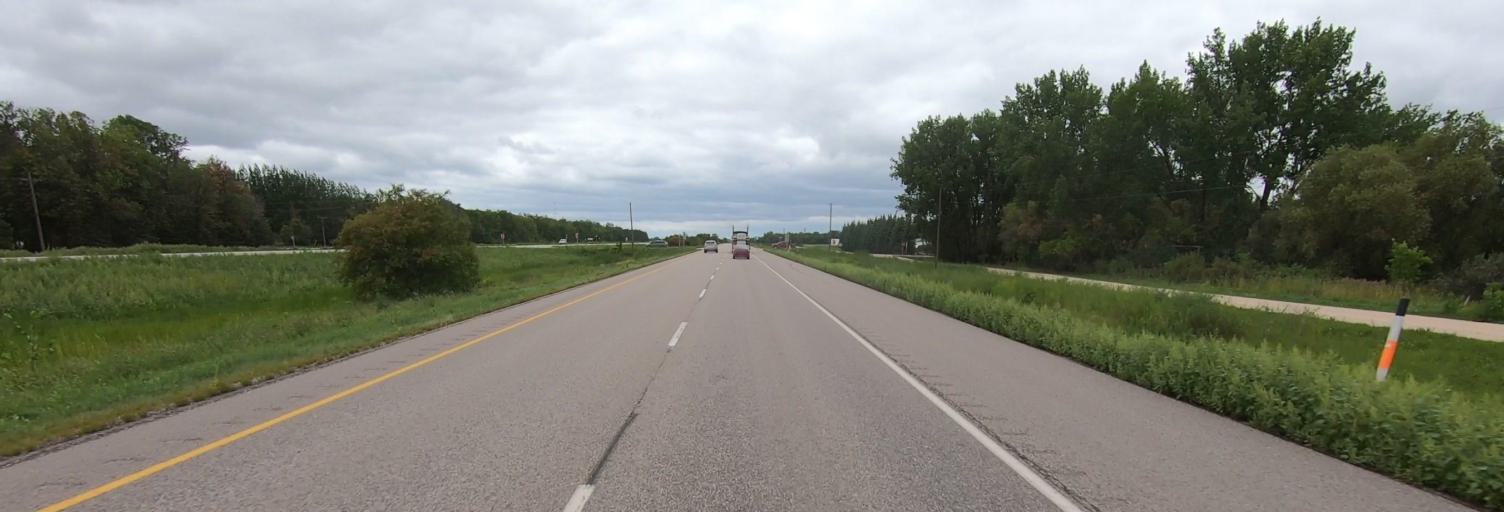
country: CA
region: Manitoba
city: Portage la Prairie
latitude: 49.9735
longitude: -98.1459
